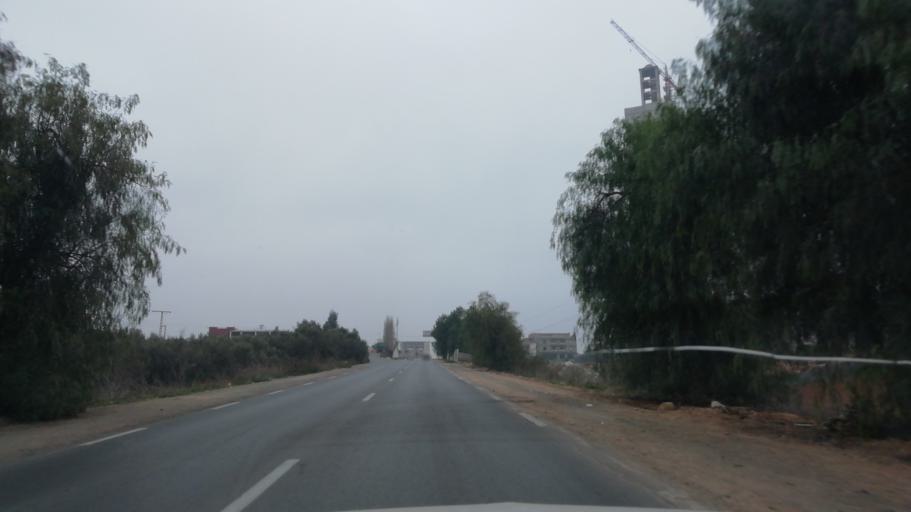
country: DZ
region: Mascara
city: Mascara
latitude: 35.4155
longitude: 0.1420
